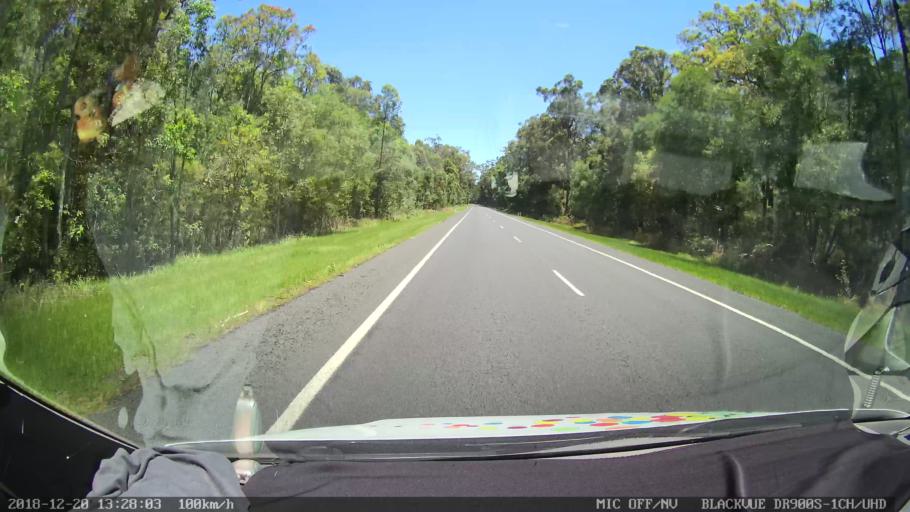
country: AU
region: New South Wales
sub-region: Clarence Valley
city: Gordon
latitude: -29.1692
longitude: 152.9923
